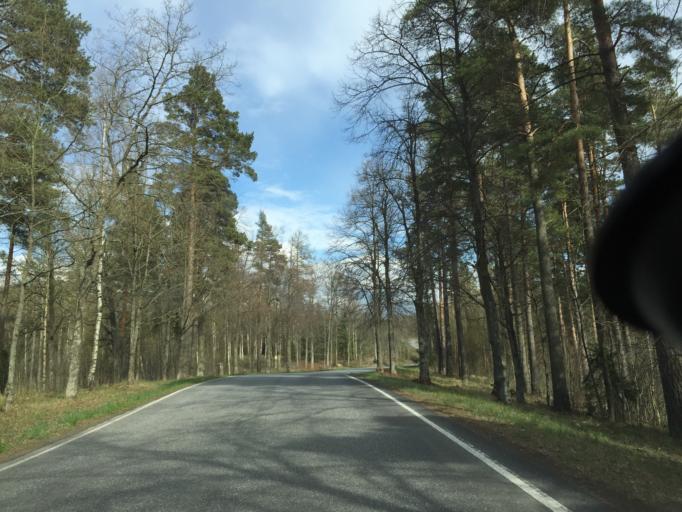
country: FI
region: Varsinais-Suomi
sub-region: Salo
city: Pernioe
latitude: 60.0343
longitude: 23.2202
